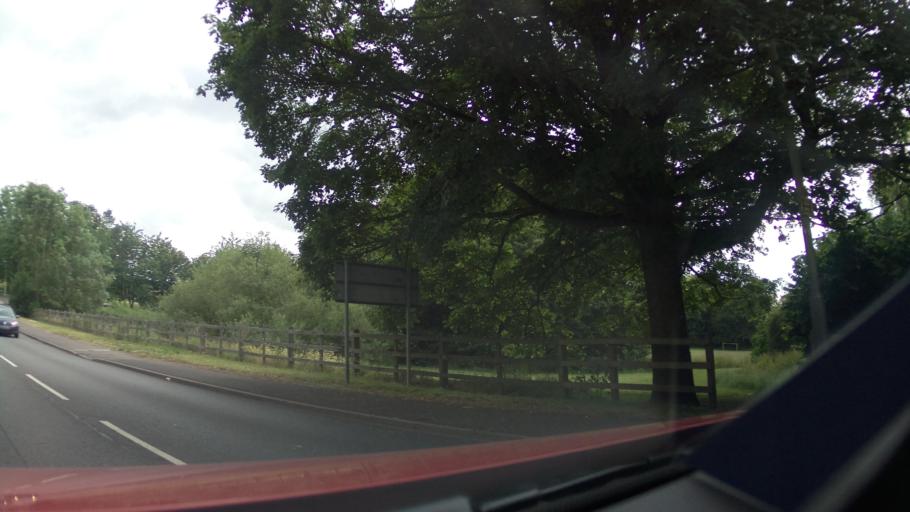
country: GB
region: England
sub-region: Dudley
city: Kingswinford
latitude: 52.5013
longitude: -2.1835
